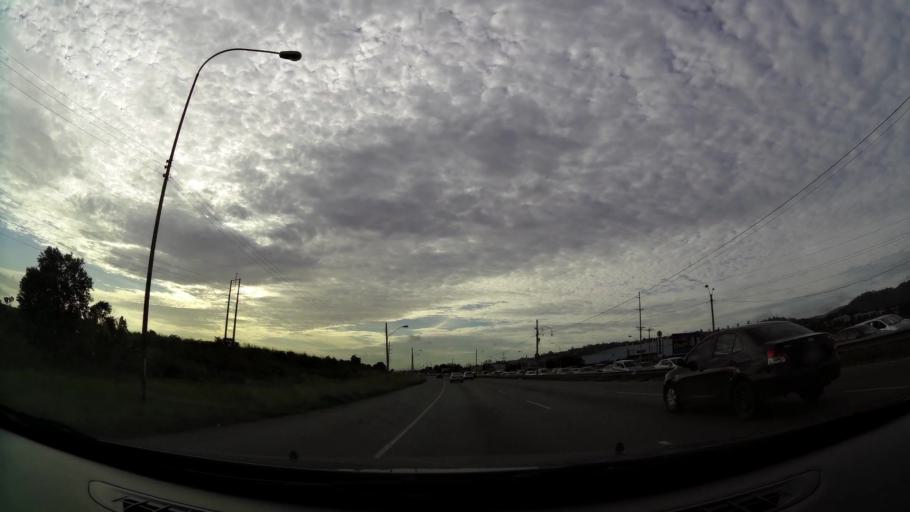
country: TT
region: San Juan/Laventille
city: Laventille
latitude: 10.6445
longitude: -61.4739
